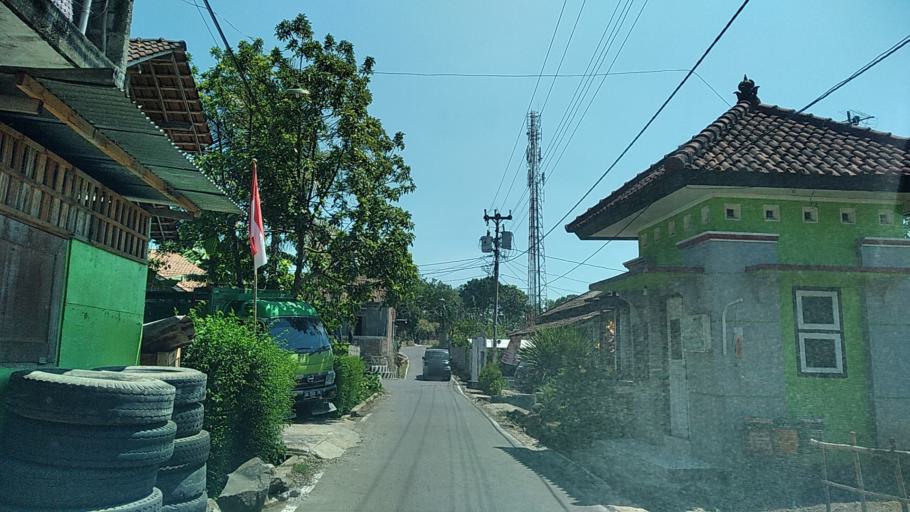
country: ID
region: Central Java
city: Ungaran
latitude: -7.1037
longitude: 110.4127
